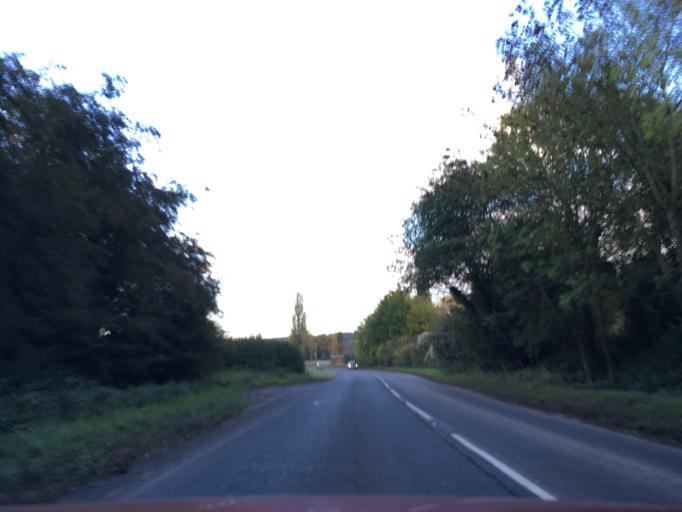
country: GB
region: England
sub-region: Herefordshire
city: Ledbury
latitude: 52.0502
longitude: -2.4618
